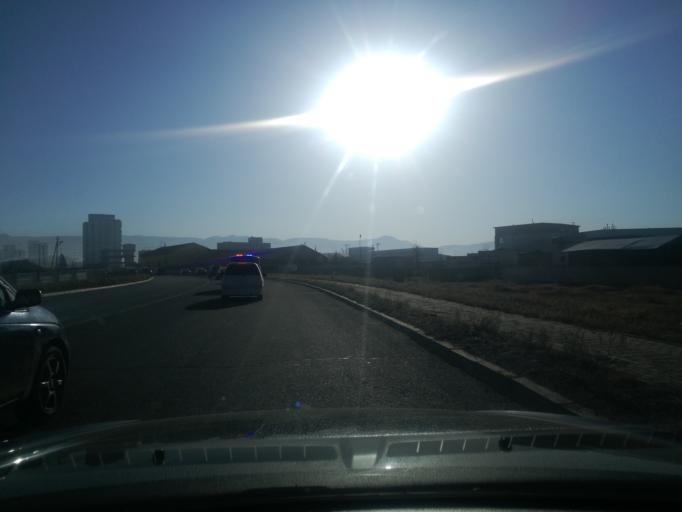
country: MN
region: Ulaanbaatar
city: Ulaanbaatar
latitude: 47.8562
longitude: 106.7543
